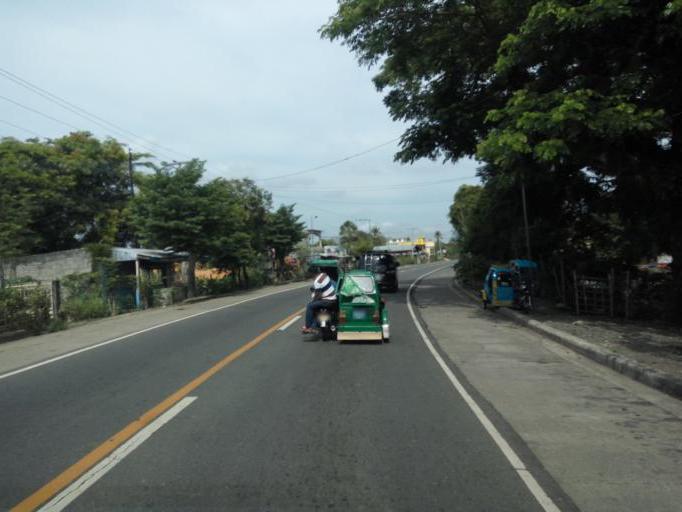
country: PH
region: Cagayan Valley
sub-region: Province of Isabela
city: Reina Mercedes
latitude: 16.9893
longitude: 121.8038
